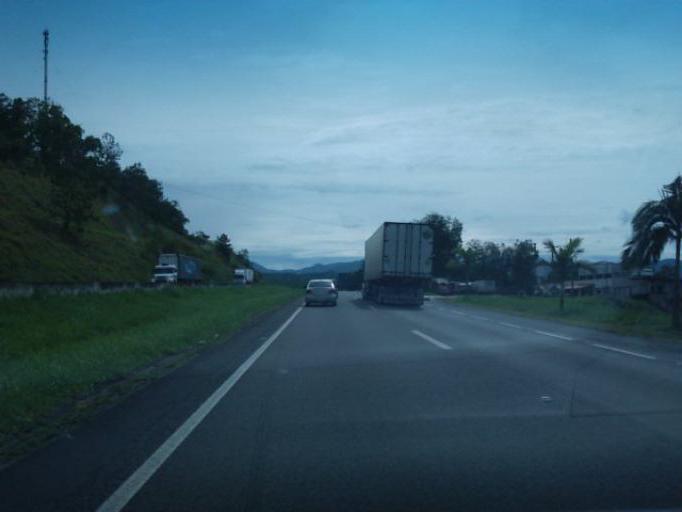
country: BR
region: Sao Paulo
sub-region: Cajati
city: Cajati
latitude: -24.7523
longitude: -48.1567
